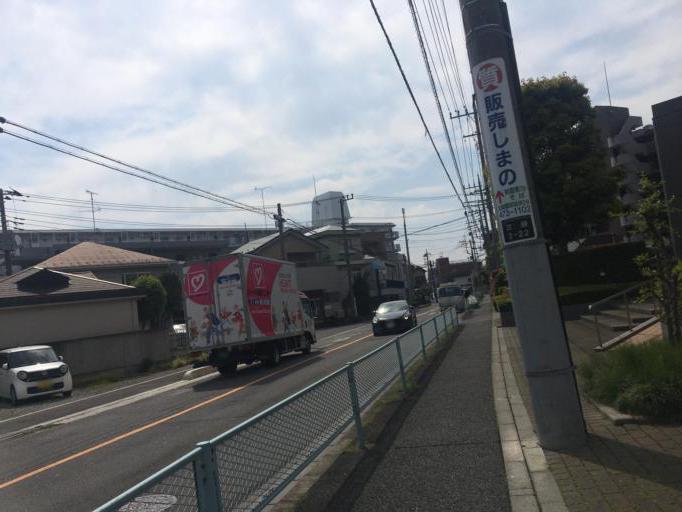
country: JP
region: Saitama
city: Shiki
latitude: 35.8173
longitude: 139.5785
